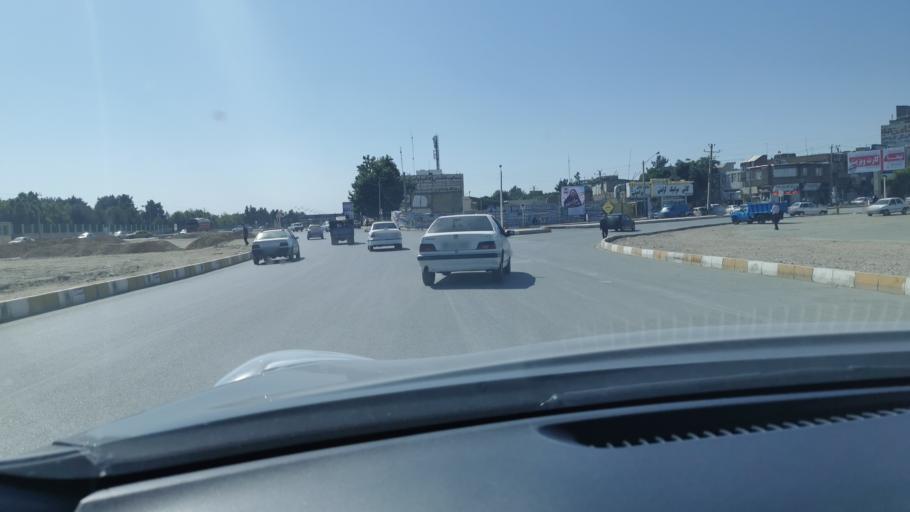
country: IR
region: Razavi Khorasan
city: Chenaran
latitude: 36.6405
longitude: 59.1180
